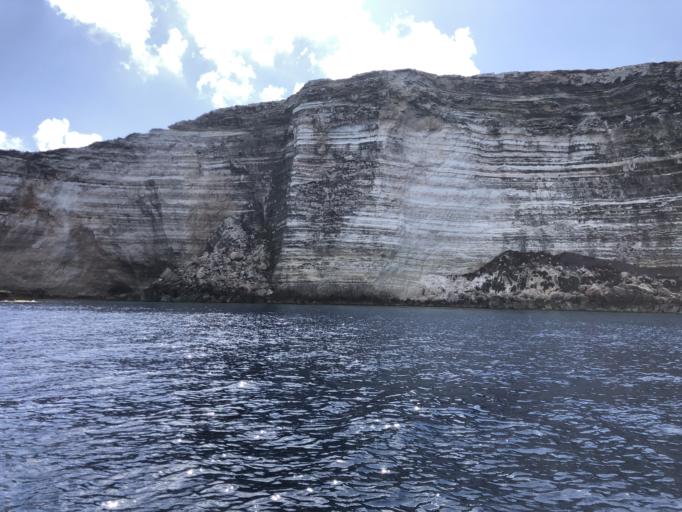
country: IT
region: Sicily
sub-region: Agrigento
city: Lampedusa
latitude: 35.5270
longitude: 12.5219
